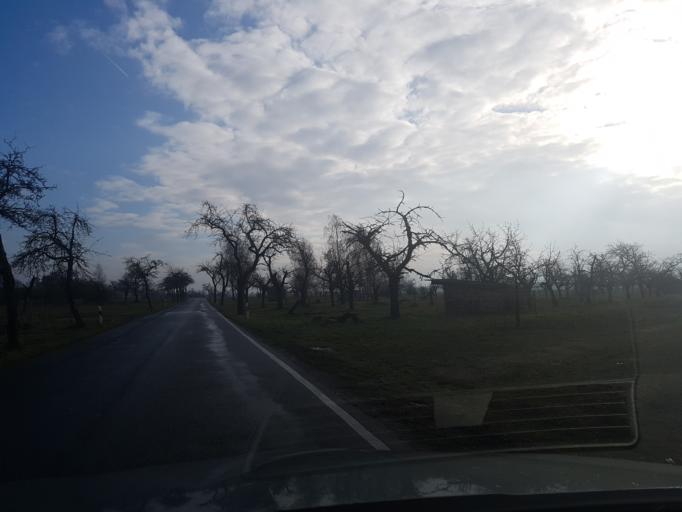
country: DE
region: Brandenburg
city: Hohenleipisch
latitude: 51.4918
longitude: 13.5665
